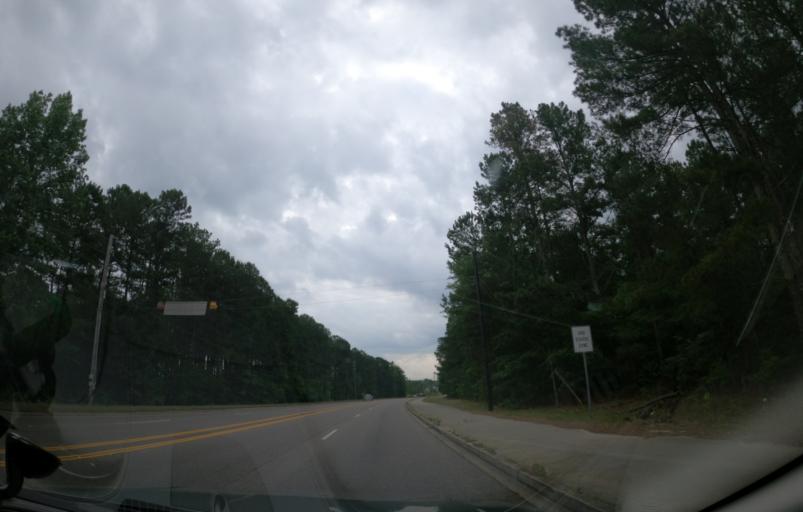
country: US
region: South Carolina
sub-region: Aiken County
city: Aiken
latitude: 33.5788
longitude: -81.7089
